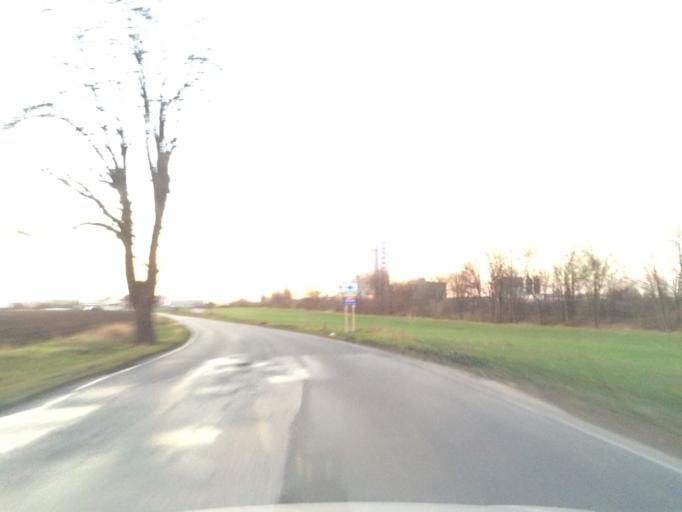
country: CZ
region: Central Bohemia
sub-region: Okres Kladno
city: Slany
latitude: 50.2256
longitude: 14.1134
